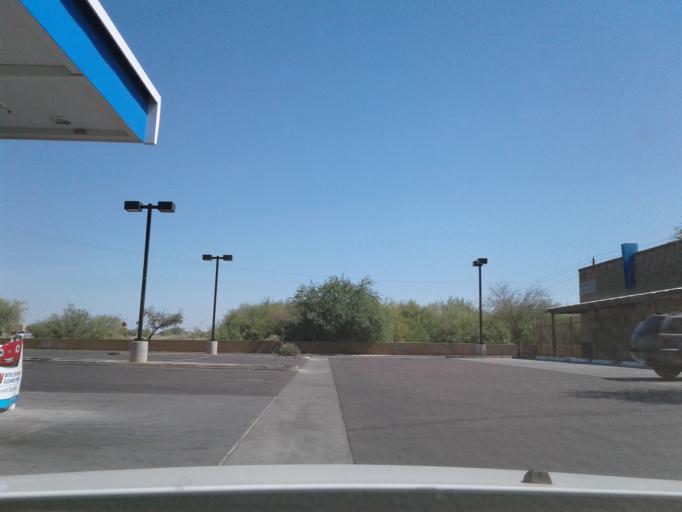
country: US
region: Arizona
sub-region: Maricopa County
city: Laveen
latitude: 33.2907
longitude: -112.1683
